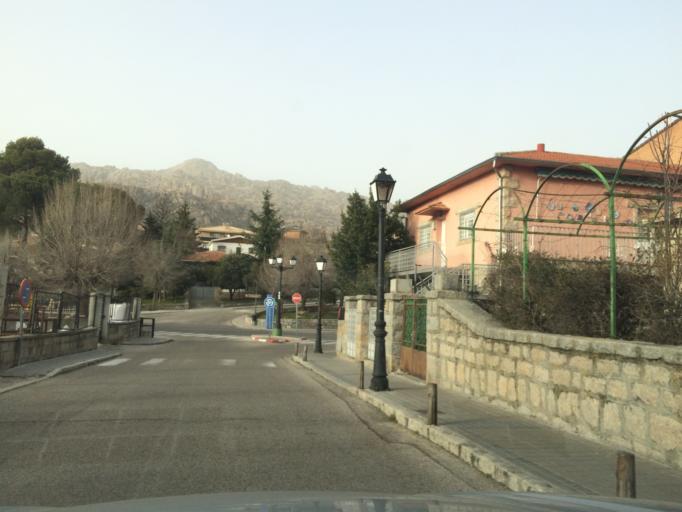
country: ES
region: Madrid
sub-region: Provincia de Madrid
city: Manzanares el Real
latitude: 40.7290
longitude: -3.8652
